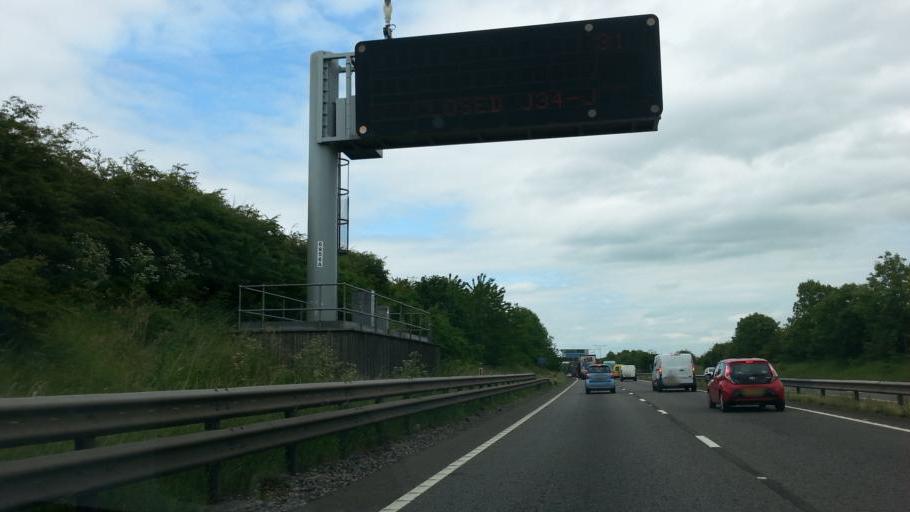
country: GB
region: England
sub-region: Leicestershire
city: Castle Donington
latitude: 52.8049
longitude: -1.3234
